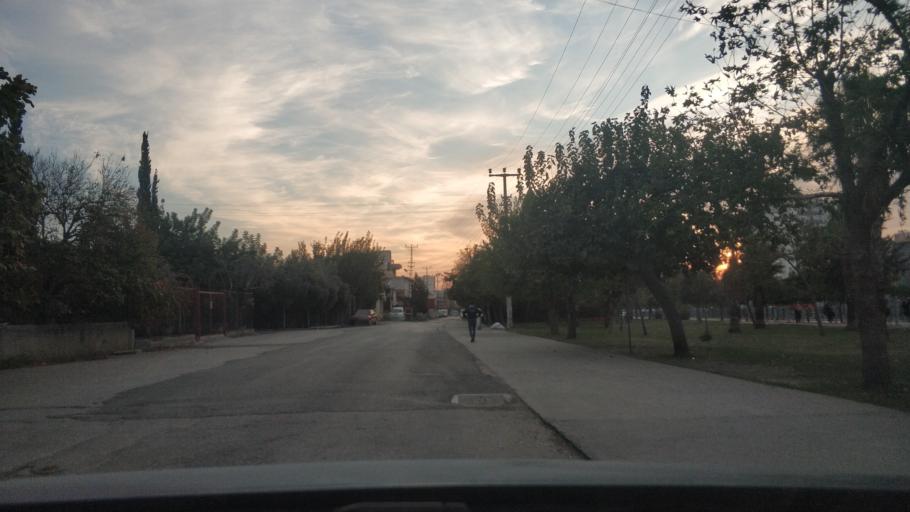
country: TR
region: Adana
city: Seyhan
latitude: 37.0117
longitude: 35.2942
